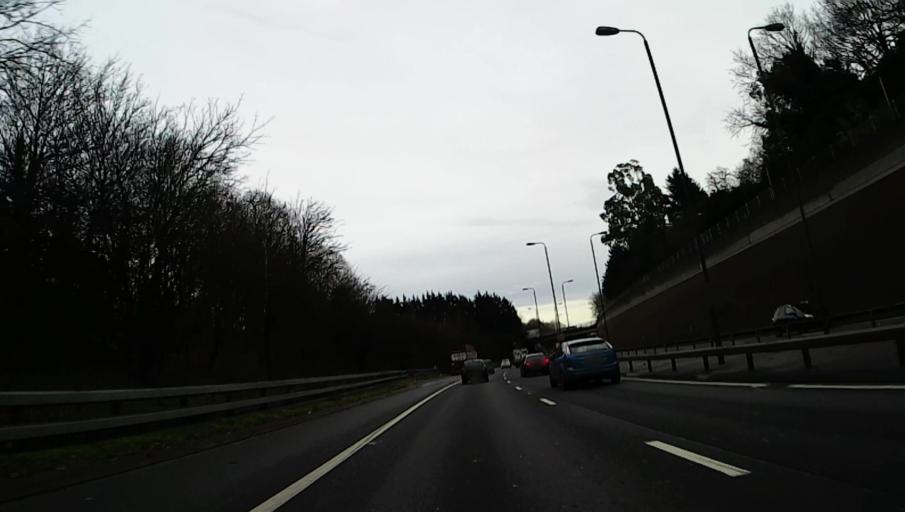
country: GB
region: England
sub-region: Greater London
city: Welling
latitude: 51.4583
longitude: 0.0764
